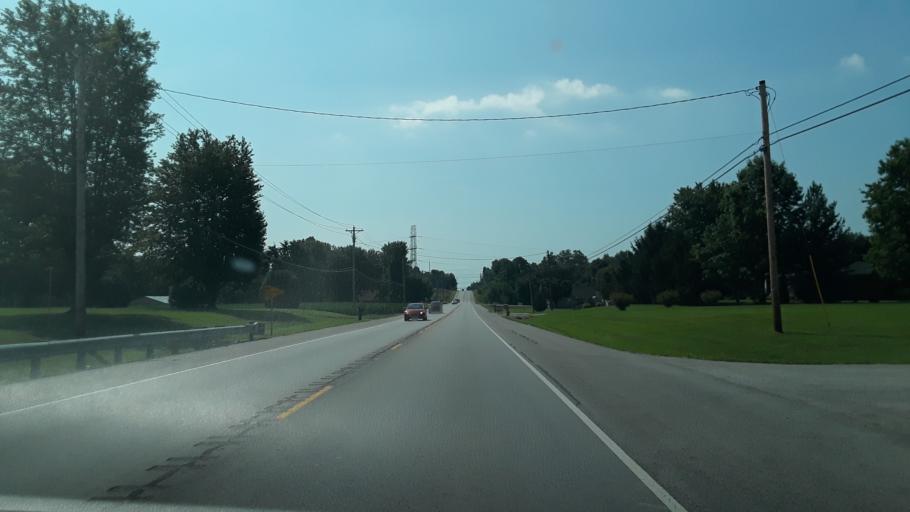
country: US
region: Indiana
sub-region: Clark County
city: Sellersburg
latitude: 38.4061
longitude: -85.7896
